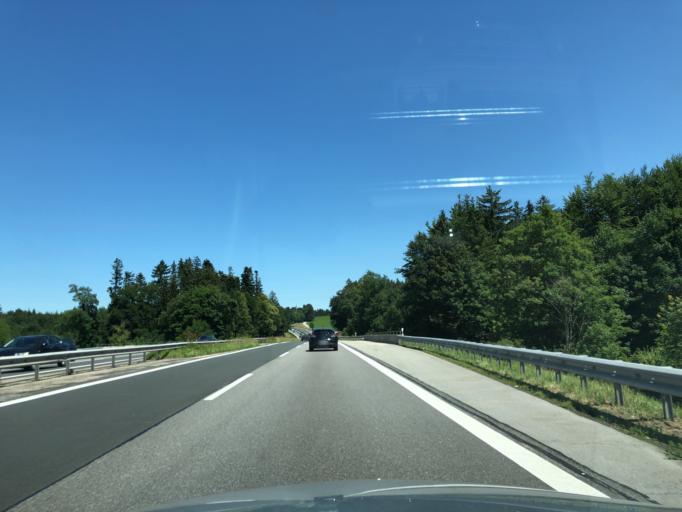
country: DE
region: Bavaria
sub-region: Upper Bavaria
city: Aschau im Chiemgau
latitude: 47.8040
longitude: 12.3253
